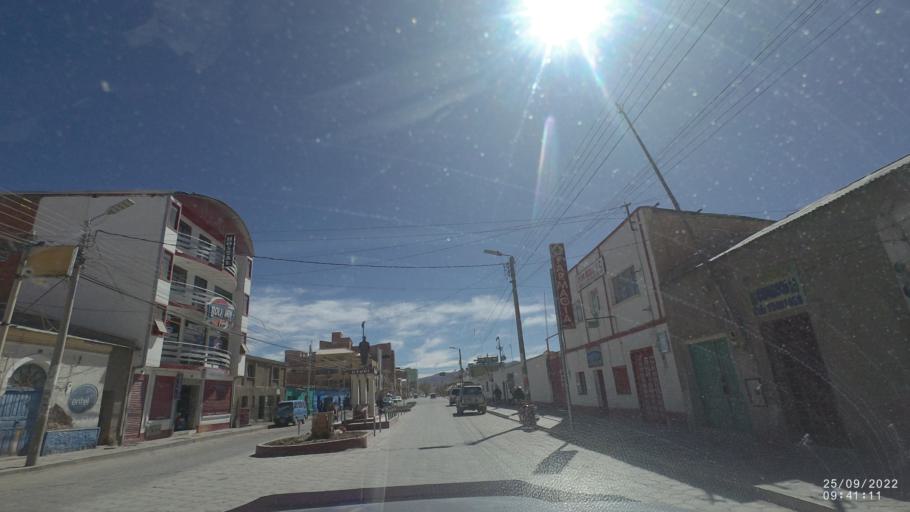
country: BO
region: Potosi
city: Uyuni
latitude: -20.4617
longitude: -66.8230
